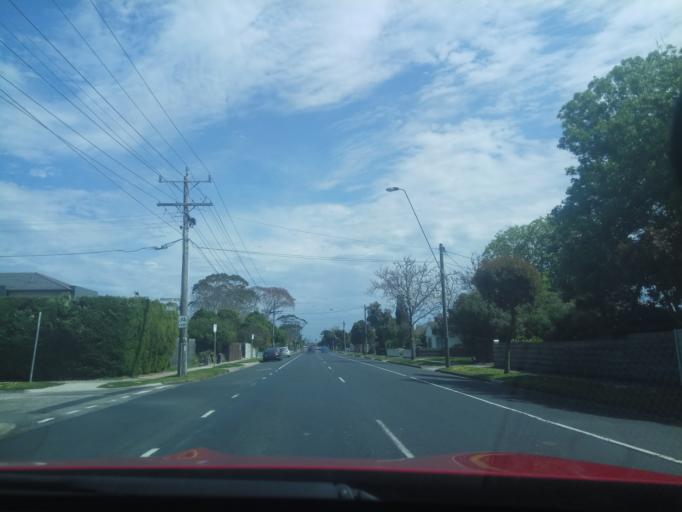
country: AU
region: Victoria
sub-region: Kingston
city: Edithvale
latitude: -38.0358
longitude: 145.1174
